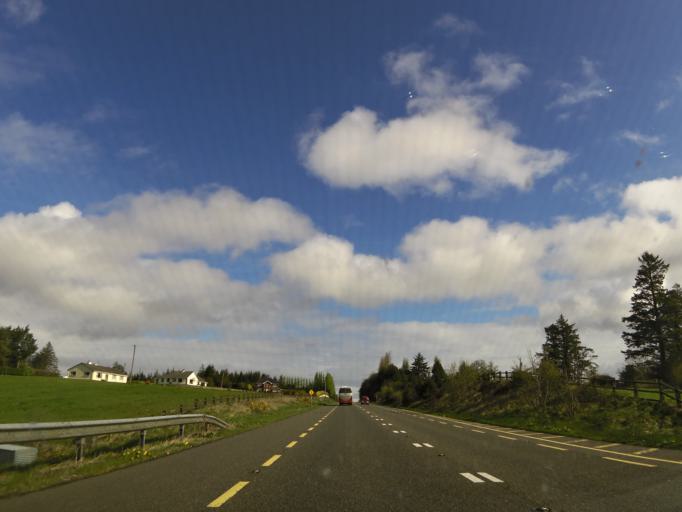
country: IE
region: Connaught
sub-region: Maigh Eo
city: Ballyhaunis
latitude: 53.8886
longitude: -8.8016
